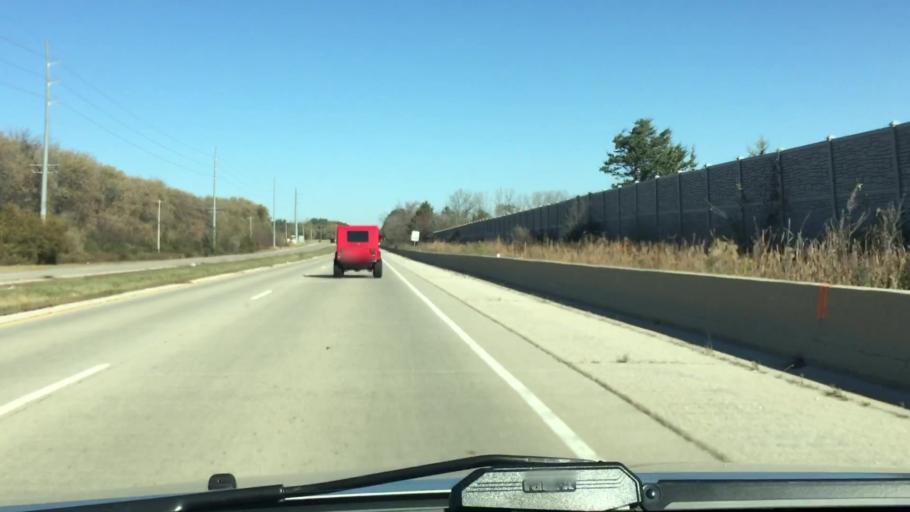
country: US
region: Wisconsin
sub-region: Waukesha County
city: Sussex
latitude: 43.1154
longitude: -88.2100
